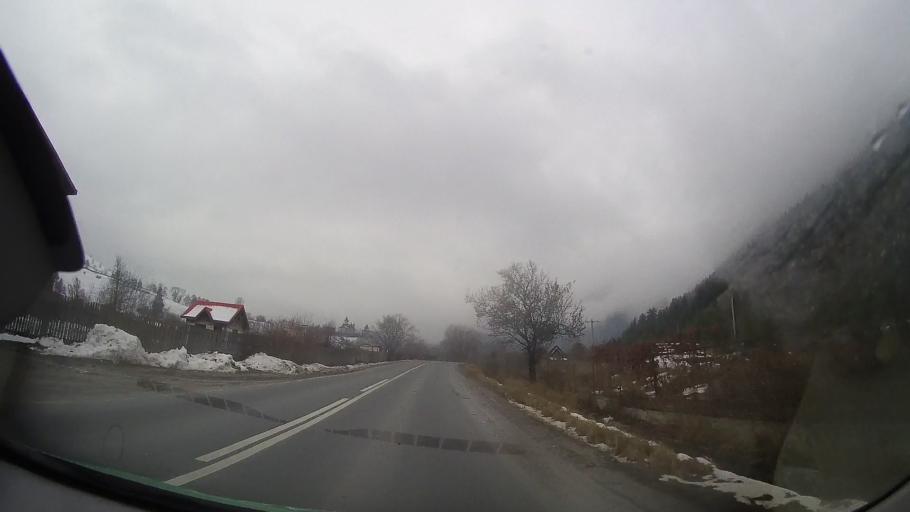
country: RO
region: Neamt
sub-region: Comuna Bicazu Ardelean
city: Bicazu Ardelean
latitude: 46.8404
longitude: 25.9073
